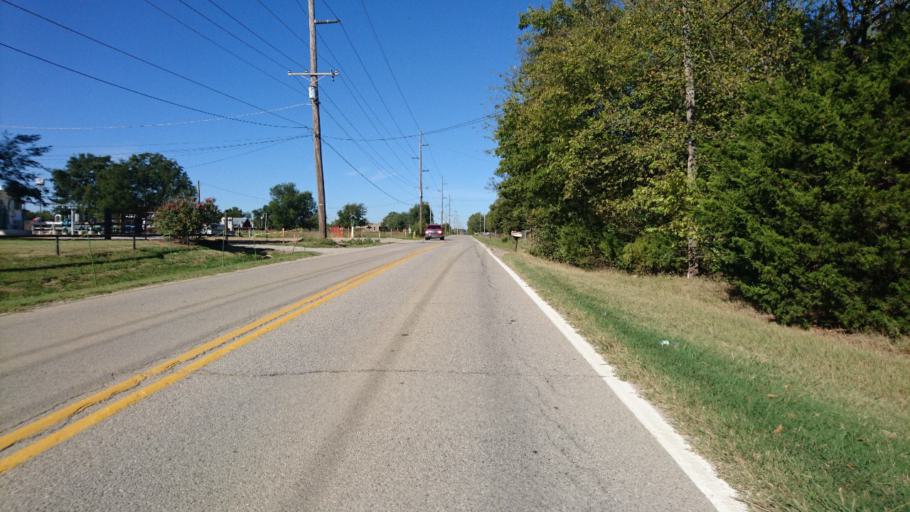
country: US
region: Oklahoma
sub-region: Rogers County
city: Catoosa
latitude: 36.1480
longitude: -95.7703
